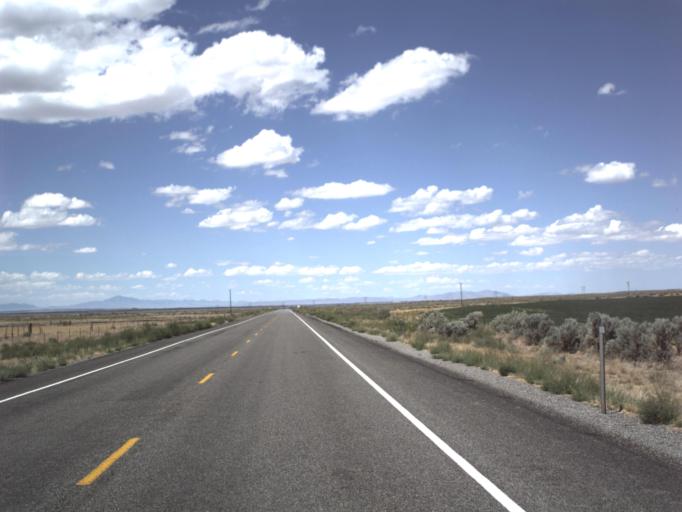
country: US
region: Utah
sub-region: Millard County
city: Fillmore
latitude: 39.1409
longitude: -112.3757
